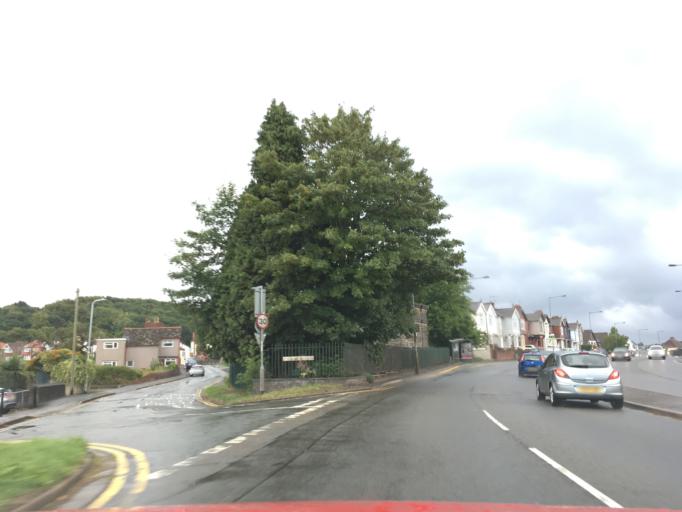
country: GB
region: Wales
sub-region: Newport
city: Newport
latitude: 51.6124
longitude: -3.0048
